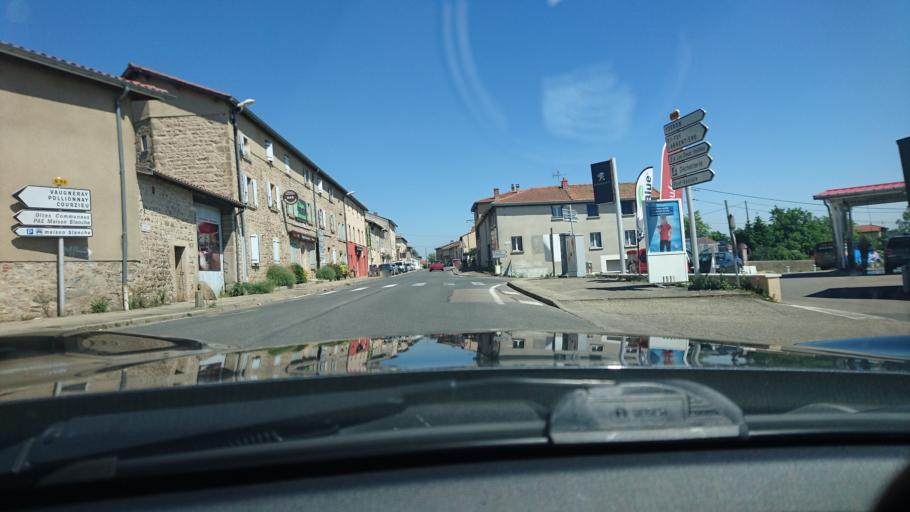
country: FR
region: Rhone-Alpes
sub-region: Departement du Rhone
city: Vaugneray
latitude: 45.7327
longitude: 4.6721
